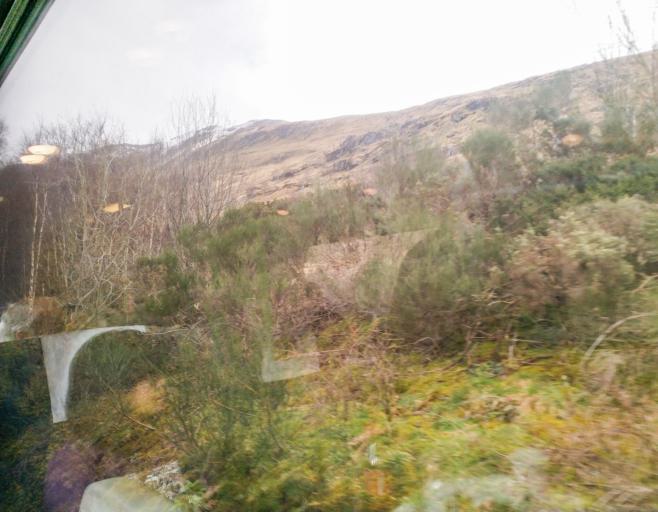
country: GB
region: Scotland
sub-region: Highland
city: Spean Bridge
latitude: 56.8172
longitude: -4.7141
